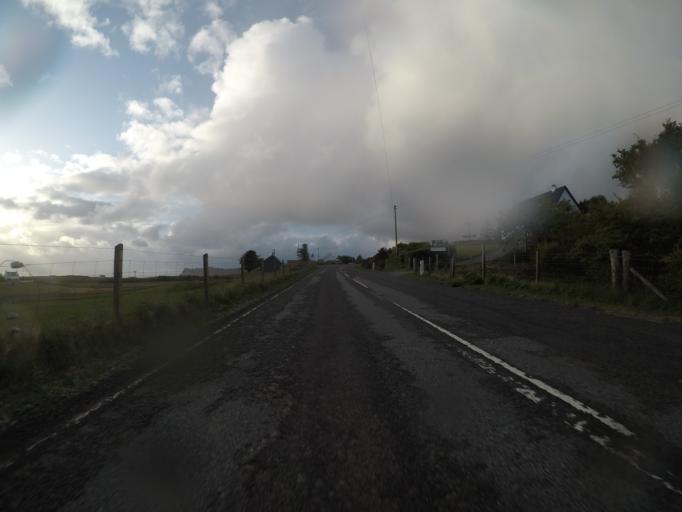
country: GB
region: Scotland
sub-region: Highland
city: Portree
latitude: 57.5650
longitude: -6.3647
